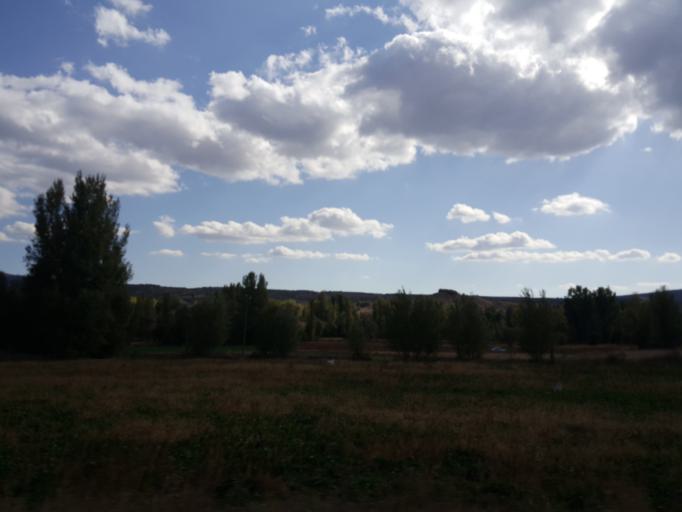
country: TR
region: Tokat
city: Sulusaray
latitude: 39.9747
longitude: 36.0352
